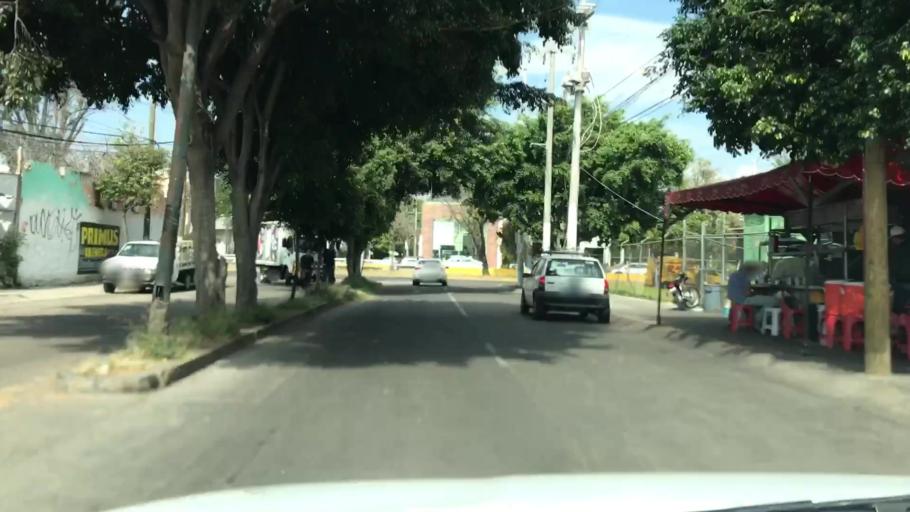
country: MX
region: Jalisco
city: Guadalajara
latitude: 20.6809
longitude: -103.4336
